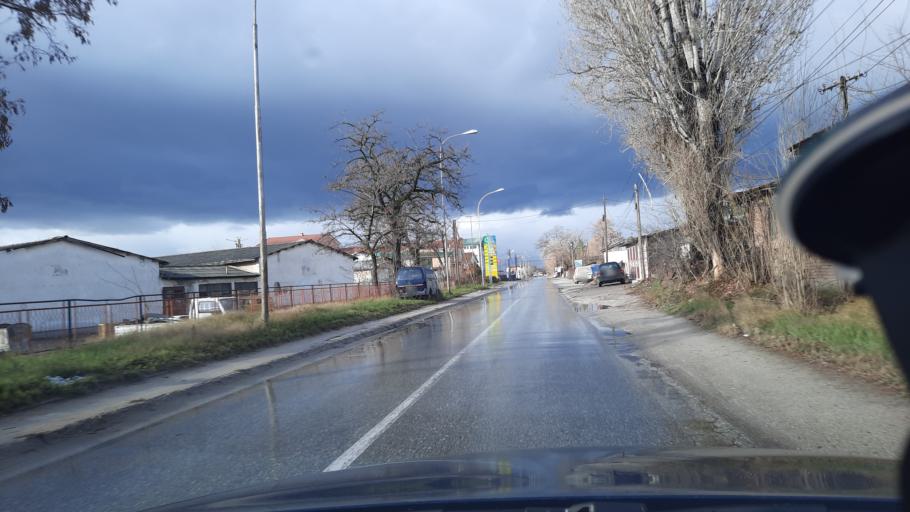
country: MK
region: Prilep
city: Markov Grad
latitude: 41.3439
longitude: 21.5349
